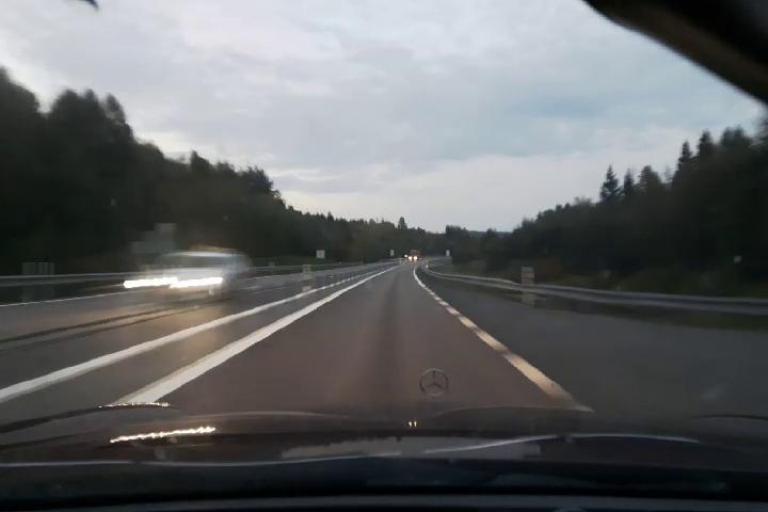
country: SE
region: Vaesternorrland
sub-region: Kramfors Kommun
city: Nordingra
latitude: 62.9551
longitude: 18.1021
